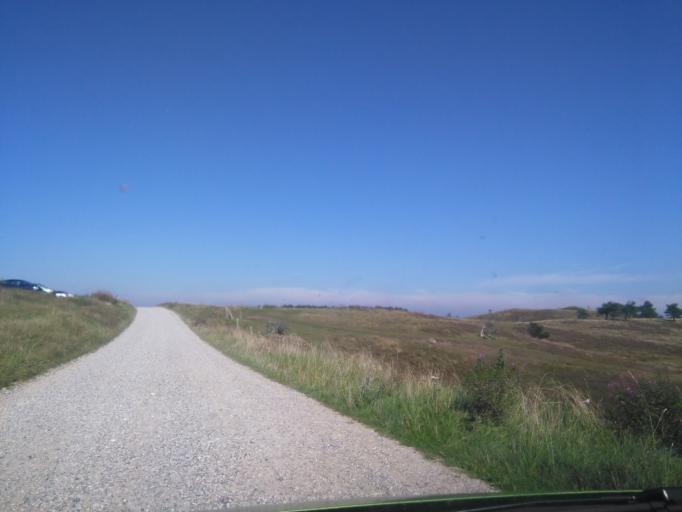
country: DK
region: Central Jutland
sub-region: Syddjurs Kommune
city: Ronde
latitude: 56.2041
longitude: 10.5325
